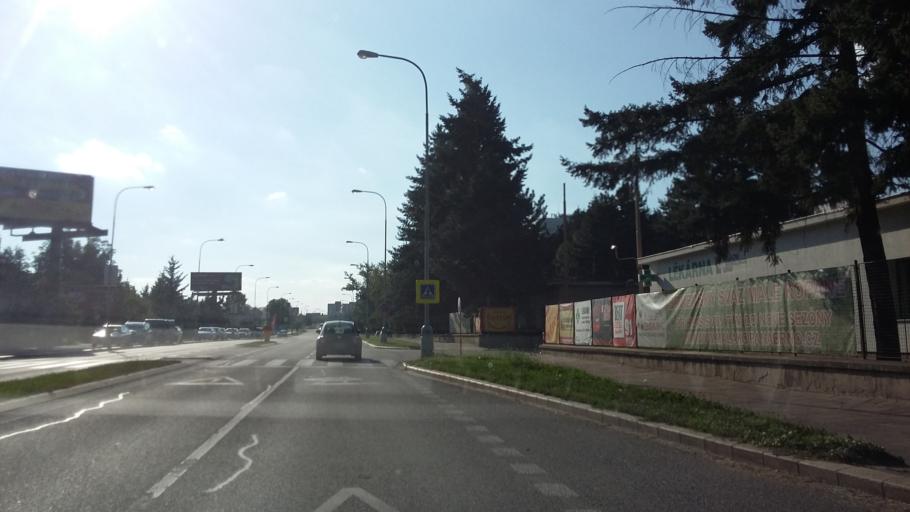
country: CZ
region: South Moravian
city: Moravany
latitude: 49.1736
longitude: 16.5772
